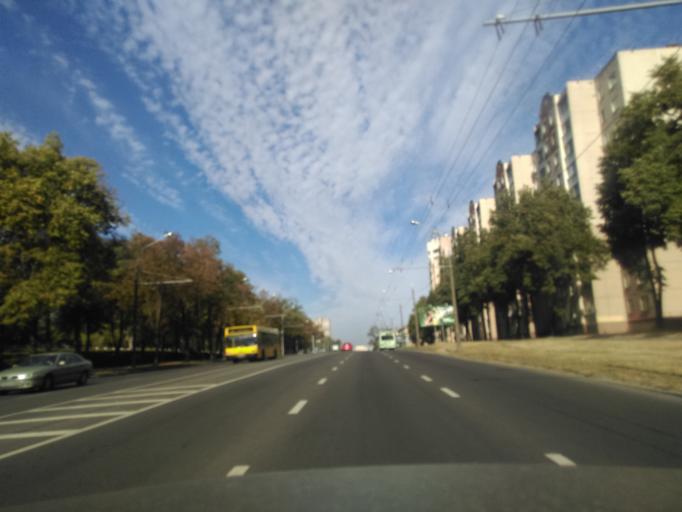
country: BY
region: Minsk
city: Minsk
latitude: 53.8822
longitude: 27.5964
